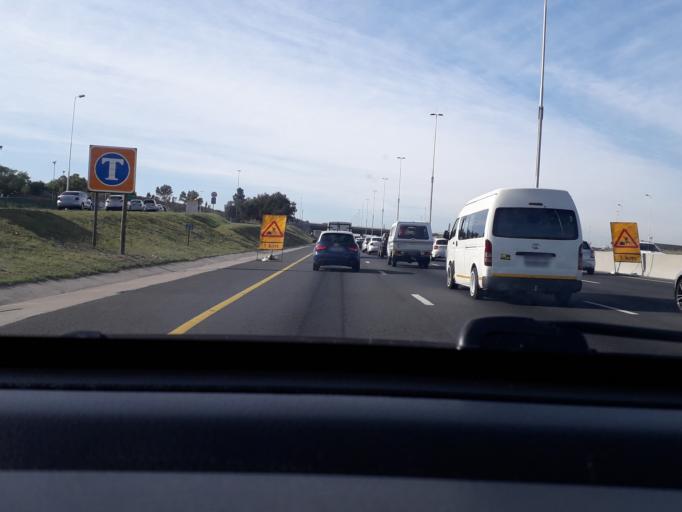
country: ZA
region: Gauteng
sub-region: City of Johannesburg Metropolitan Municipality
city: Modderfontein
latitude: -26.0785
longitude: 28.1137
